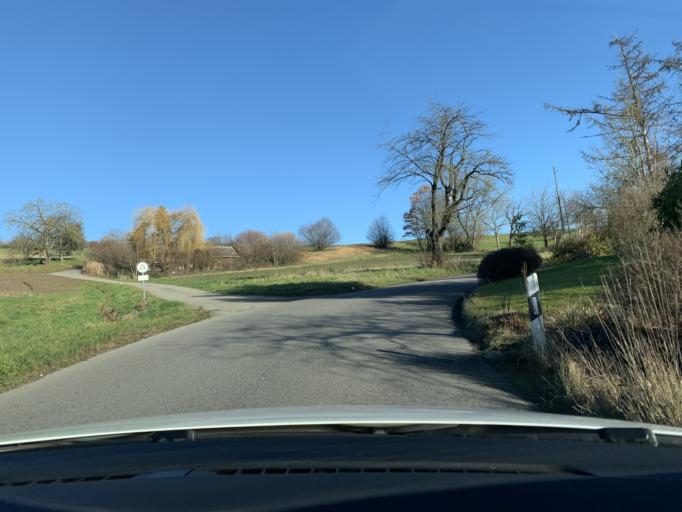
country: CH
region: Zurich
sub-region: Bezirk Dielsdorf
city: Sonnhalde
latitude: 47.4624
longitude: 8.4446
